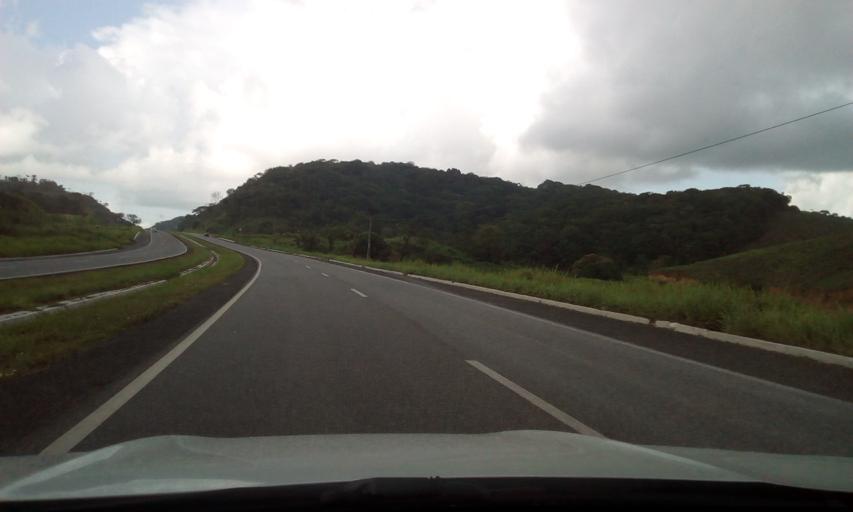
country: BR
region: Pernambuco
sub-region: Cabo De Santo Agostinho
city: Cabo
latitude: -8.2592
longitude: -35.0454
